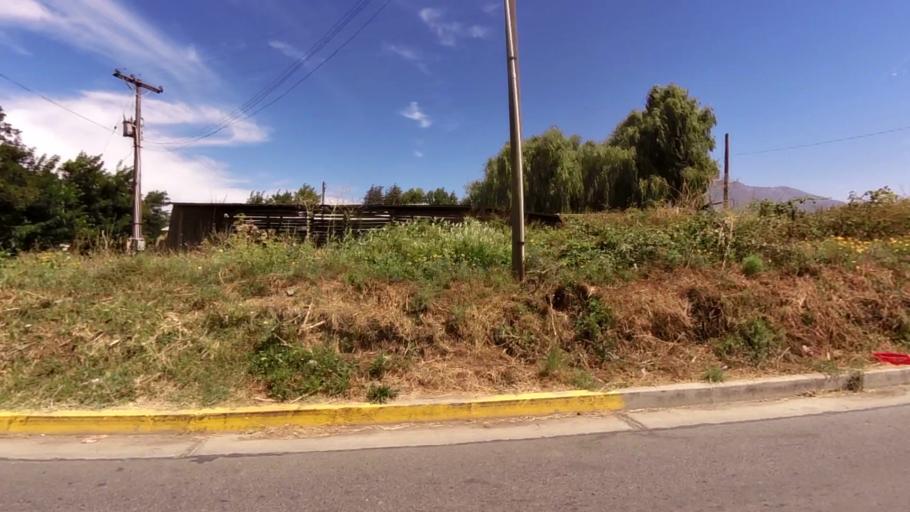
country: CL
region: O'Higgins
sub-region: Provincia de Cachapoal
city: Graneros
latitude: -34.0632
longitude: -70.7204
